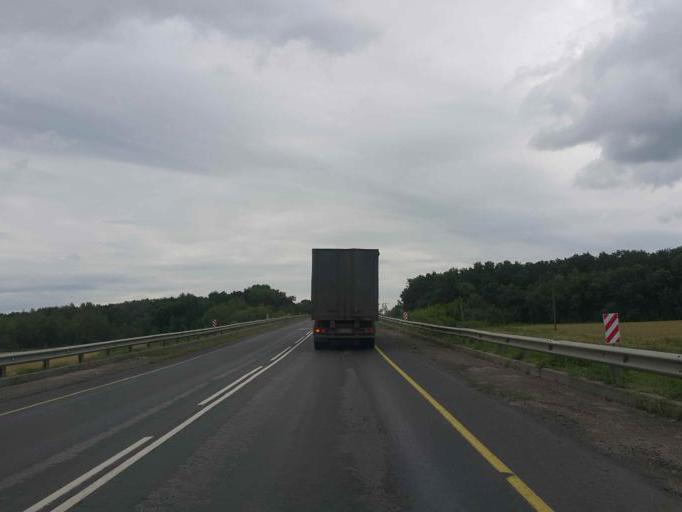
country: RU
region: Tambov
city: Zavoronezhskoye
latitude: 52.9202
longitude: 40.6233
